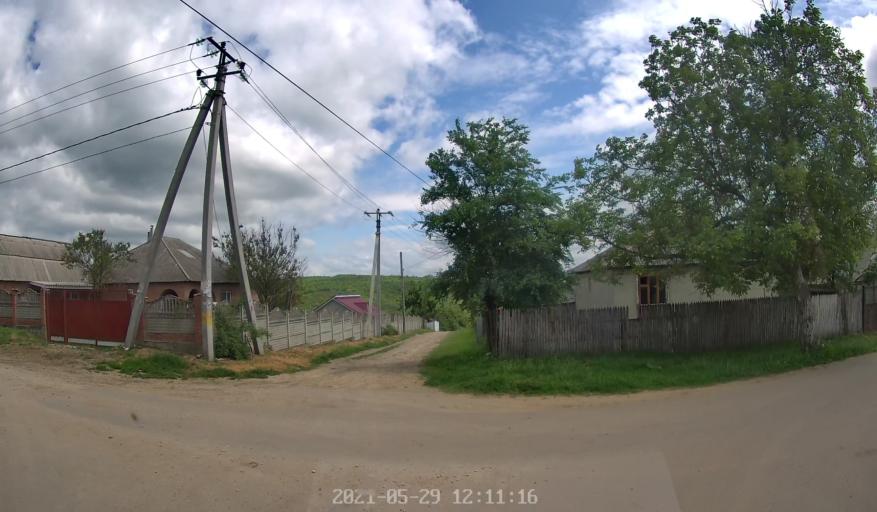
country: MD
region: Hincesti
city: Hincesti
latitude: 46.8832
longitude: 28.6293
